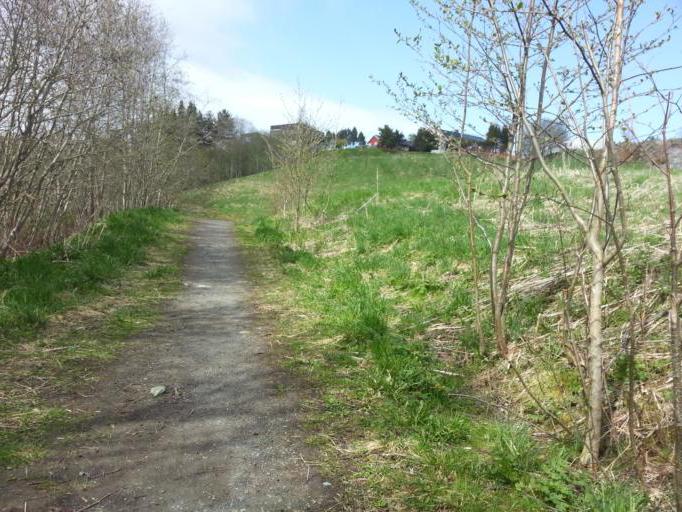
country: NO
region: Sor-Trondelag
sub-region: Trondheim
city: Trondheim
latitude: 63.3924
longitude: 10.3581
